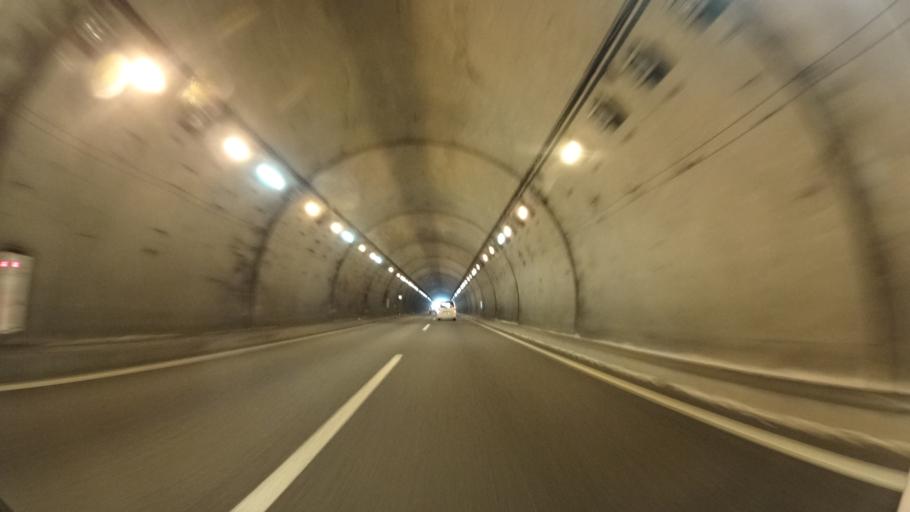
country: JP
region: Ehime
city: Saijo
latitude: 33.8863
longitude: 133.1529
